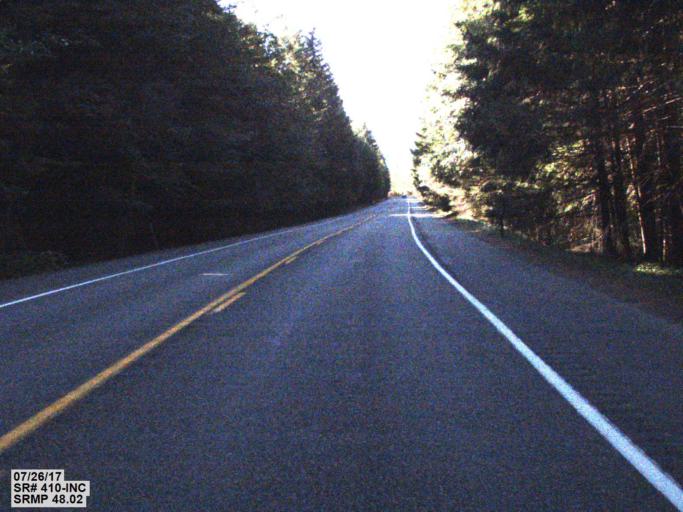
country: US
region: Washington
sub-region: King County
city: Riverbend
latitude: 47.1001
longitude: -121.5892
